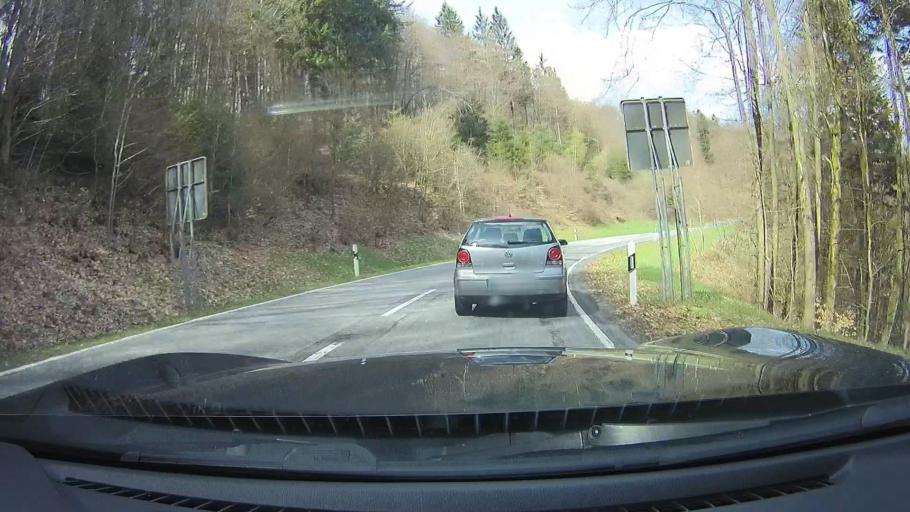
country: DE
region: Hesse
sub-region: Regierungsbezirk Darmstadt
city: Hesseneck
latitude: 49.5785
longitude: 9.0236
